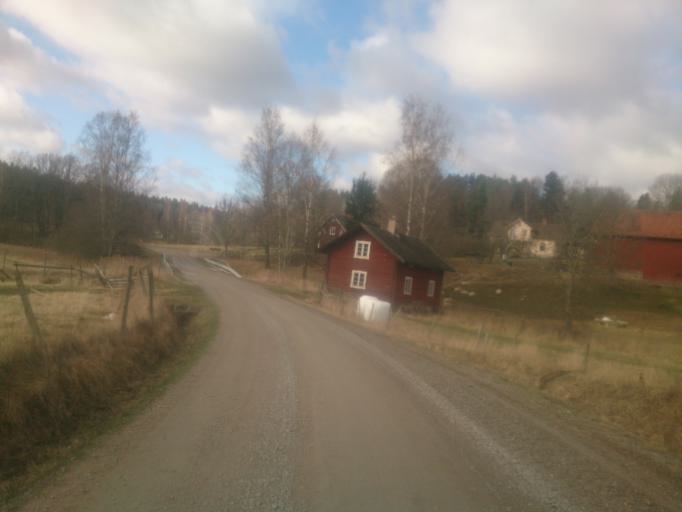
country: SE
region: OEstergoetland
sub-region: Atvidabergs Kommun
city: Atvidaberg
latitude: 58.2108
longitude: 16.1677
